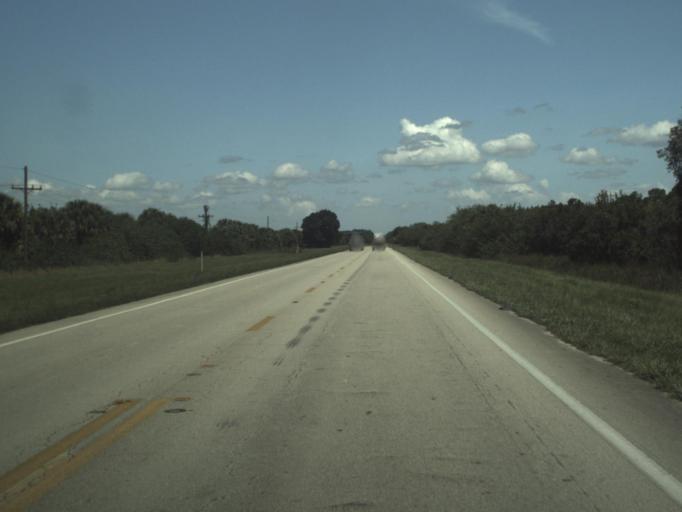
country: US
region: Florida
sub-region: Martin County
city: Indiantown
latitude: 26.9882
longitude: -80.4193
